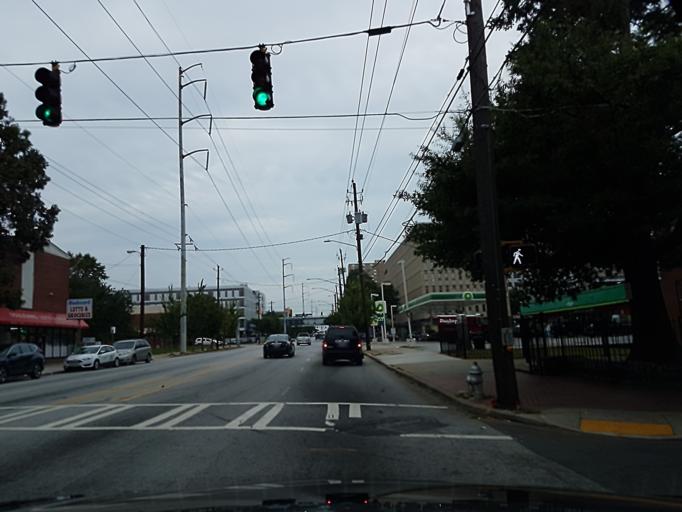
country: US
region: Georgia
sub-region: Fulton County
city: Atlanta
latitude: 33.7649
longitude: -84.3720
